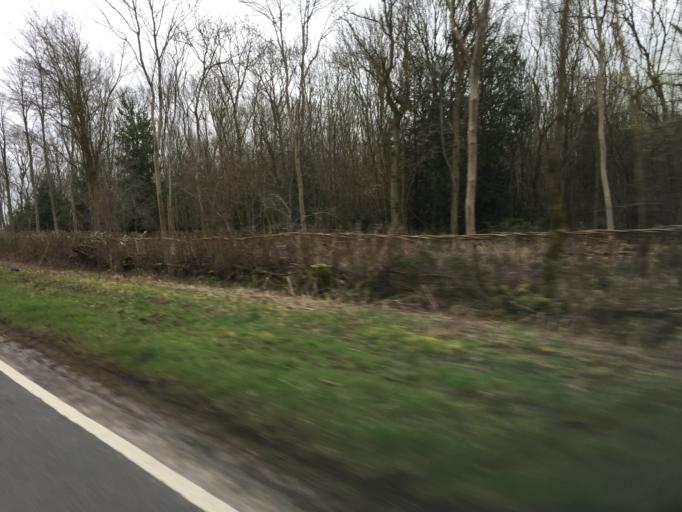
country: GB
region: England
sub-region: Oxfordshire
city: Faringdon
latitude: 51.6707
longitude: -1.6191
